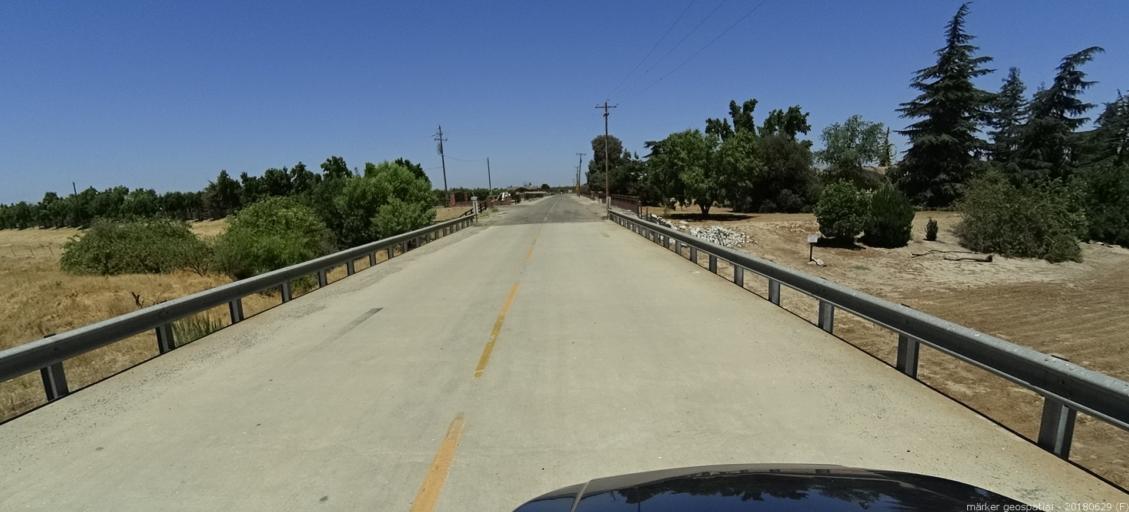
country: US
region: California
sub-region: Madera County
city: Parksdale
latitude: 36.9962
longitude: -120.0022
